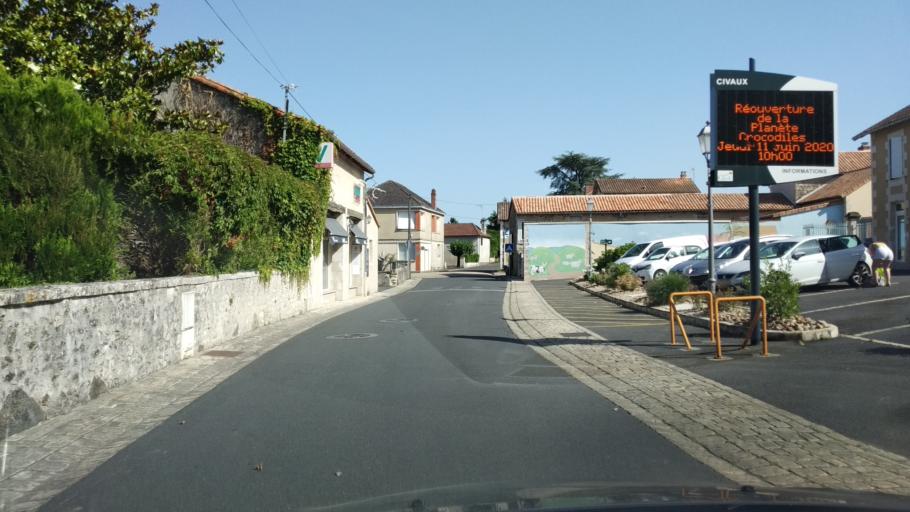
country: FR
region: Poitou-Charentes
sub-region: Departement de la Vienne
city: Lussac-les-Chateaux
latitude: 46.4444
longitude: 0.6660
